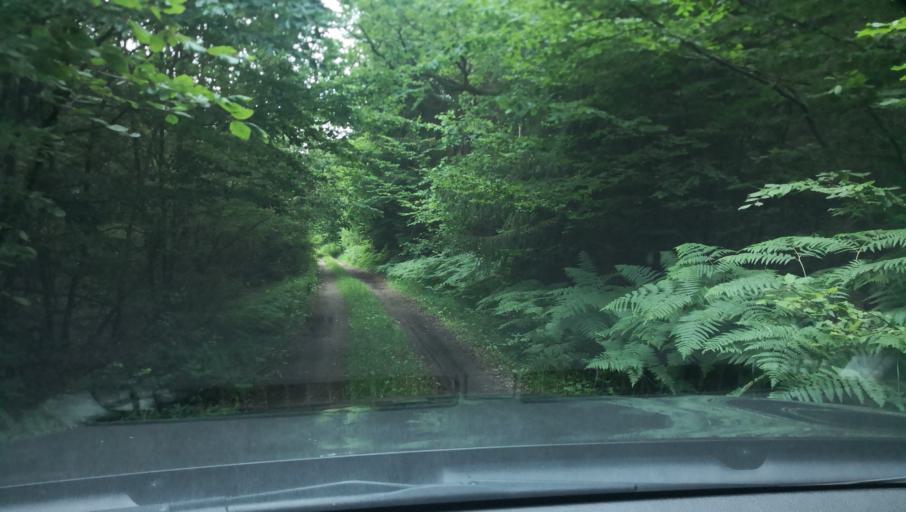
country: SE
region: Skane
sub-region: Simrishamns Kommun
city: Kivik
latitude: 55.6175
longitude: 14.1077
